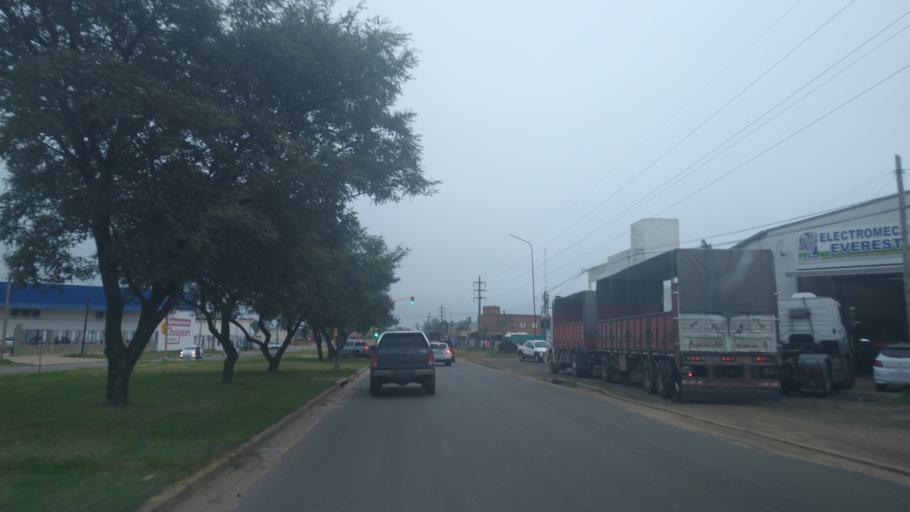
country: AR
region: Entre Rios
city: Chajari
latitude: -30.7618
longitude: -58.0105
